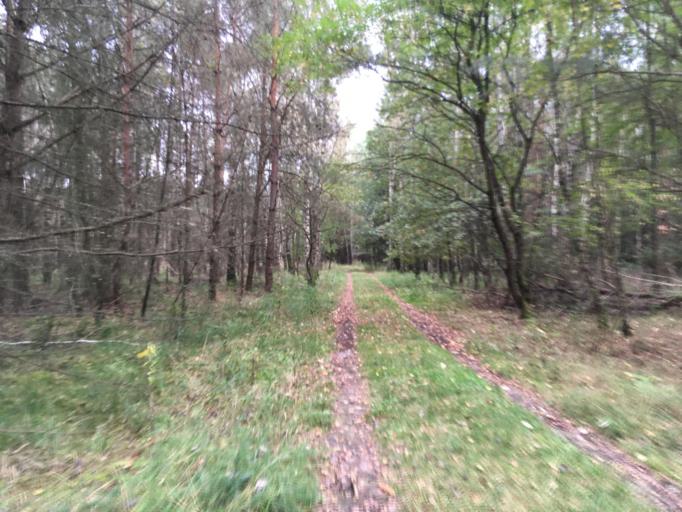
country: DE
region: Brandenburg
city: Glienicke
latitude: 52.6943
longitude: 13.3481
